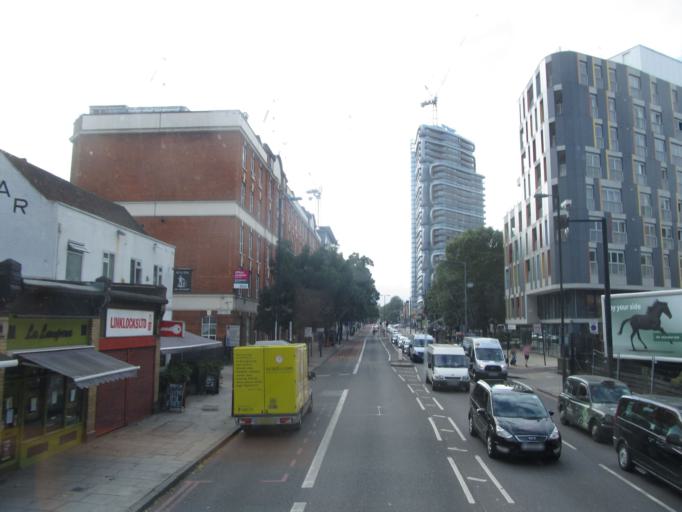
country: GB
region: England
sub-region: Greater London
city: Barbican
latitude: 51.5284
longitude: -0.0921
